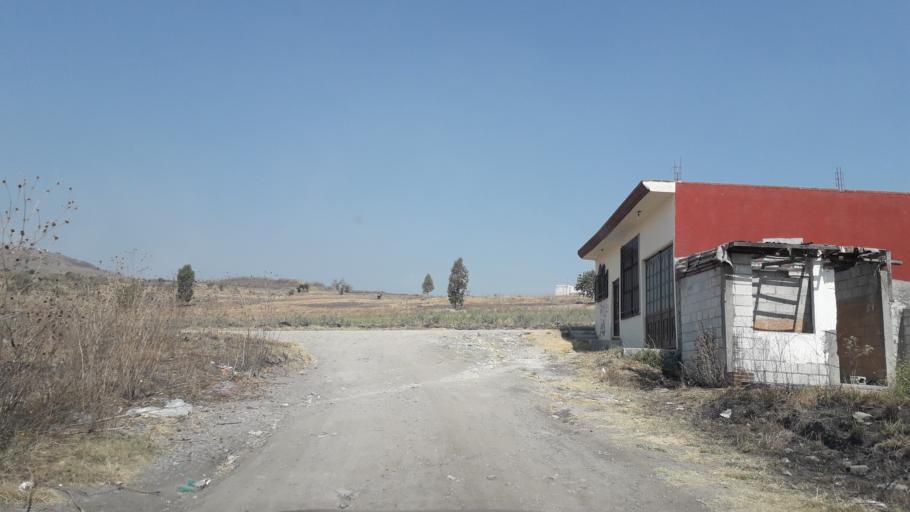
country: MX
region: Puebla
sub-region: Puebla
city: El Capulo (La Quebradora)
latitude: 18.9343
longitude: -98.2699
